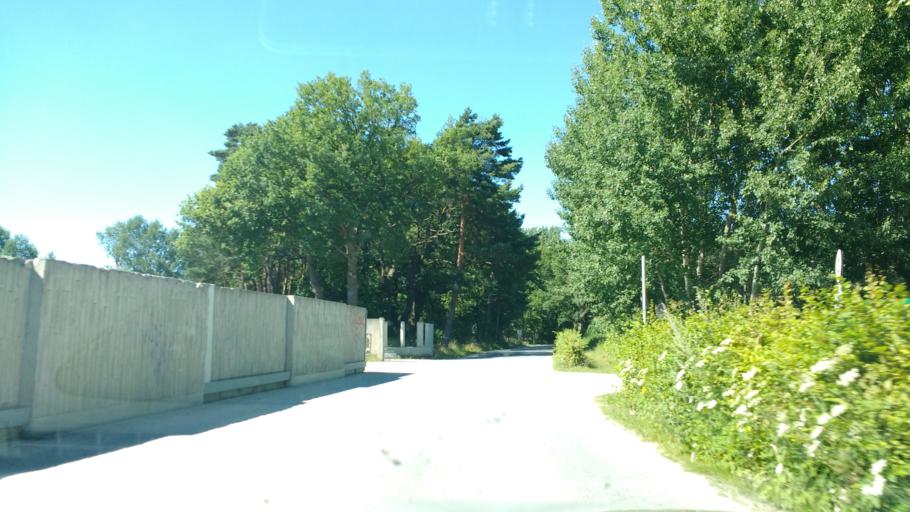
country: DE
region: North Rhine-Westphalia
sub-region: Regierungsbezirk Arnsberg
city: Lippstadt
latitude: 51.6989
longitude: 8.4070
